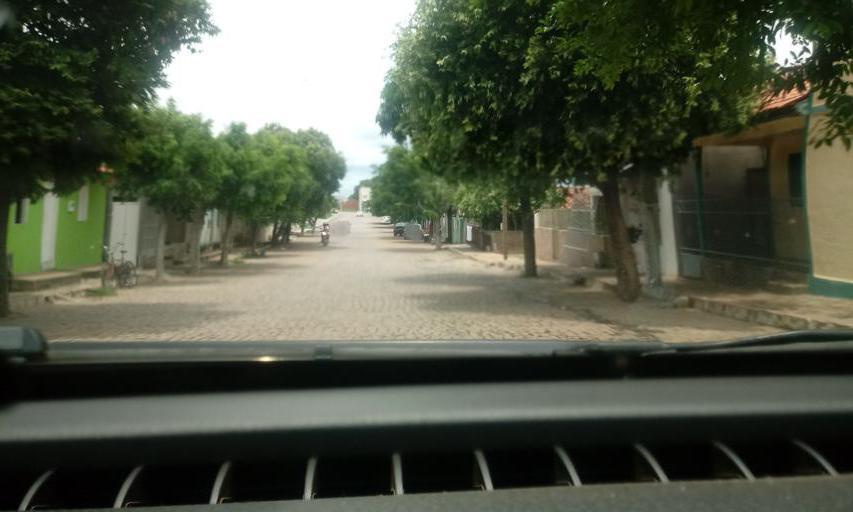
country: BR
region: Bahia
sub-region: Riacho De Santana
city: Riacho de Santana
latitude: -13.9093
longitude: -42.8451
